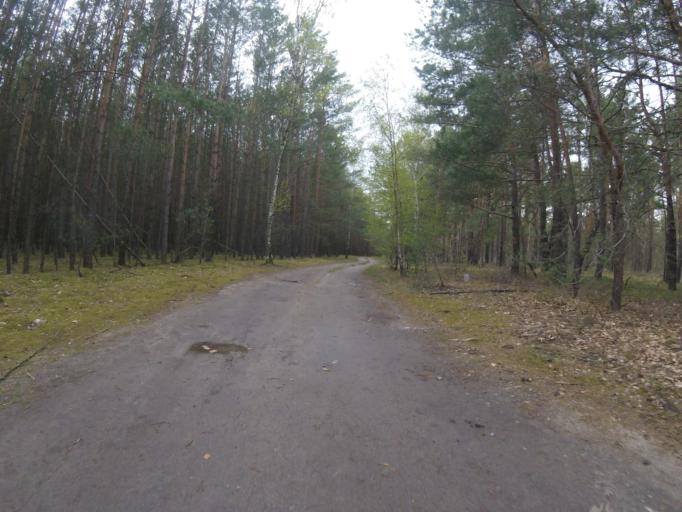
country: DE
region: Brandenburg
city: Bestensee
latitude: 52.2218
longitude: 13.6660
